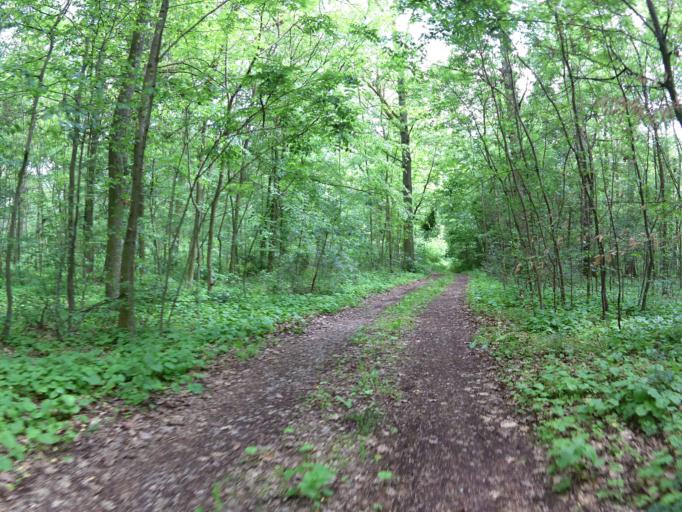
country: DE
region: Bavaria
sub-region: Regierungsbezirk Unterfranken
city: Theilheim
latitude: 49.7332
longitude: 10.0513
